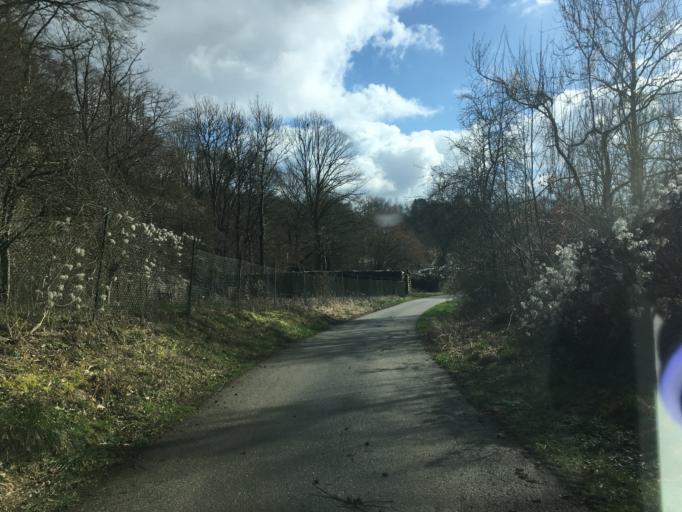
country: BE
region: Wallonia
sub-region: Province de Namur
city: Couvin
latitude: 50.0946
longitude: 4.5882
